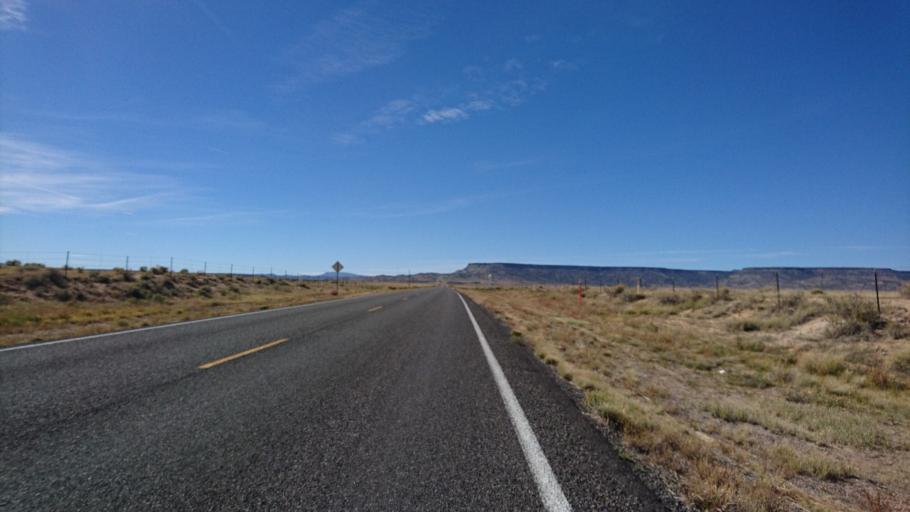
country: US
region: New Mexico
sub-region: Cibola County
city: Skyline-Ganipa
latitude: 35.0825
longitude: -107.6069
